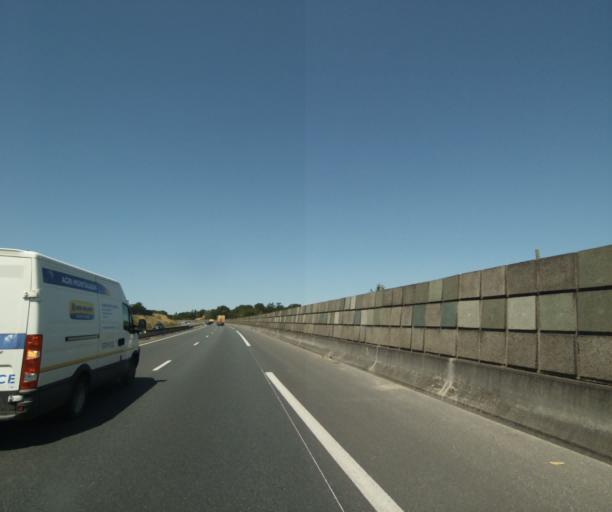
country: FR
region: Midi-Pyrenees
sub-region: Departement du Tarn-et-Garonne
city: Montauban
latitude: 44.0106
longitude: 1.3858
